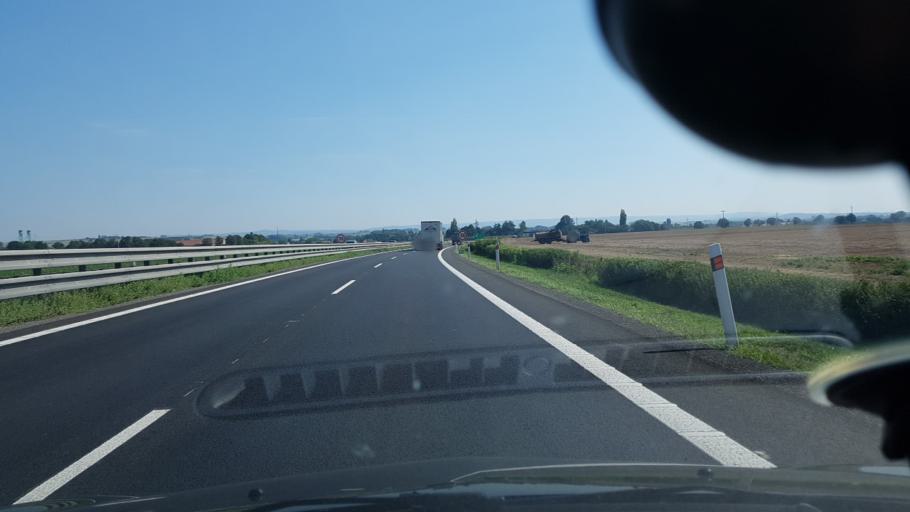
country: CZ
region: Olomoucky
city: Lutin
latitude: 49.5270
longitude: 17.1592
